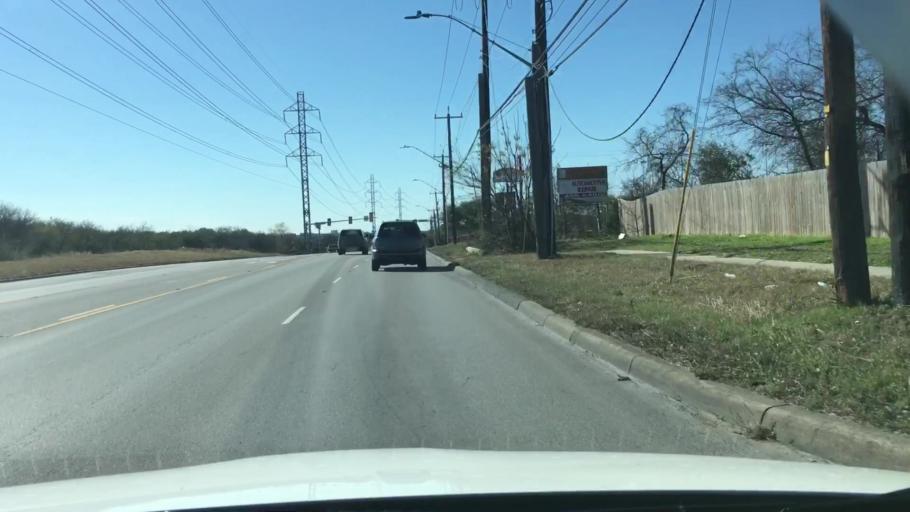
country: US
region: Texas
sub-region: Bexar County
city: Windcrest
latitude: 29.5515
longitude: -98.4301
